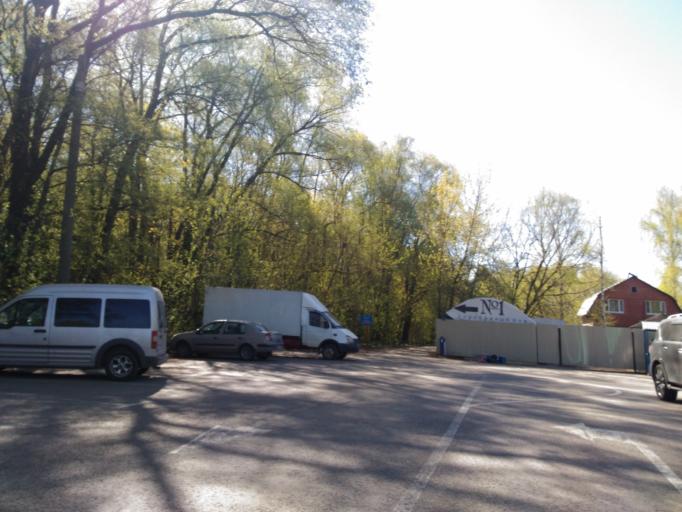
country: RU
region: Moscow
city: Strogino
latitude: 55.7791
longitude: 37.4066
